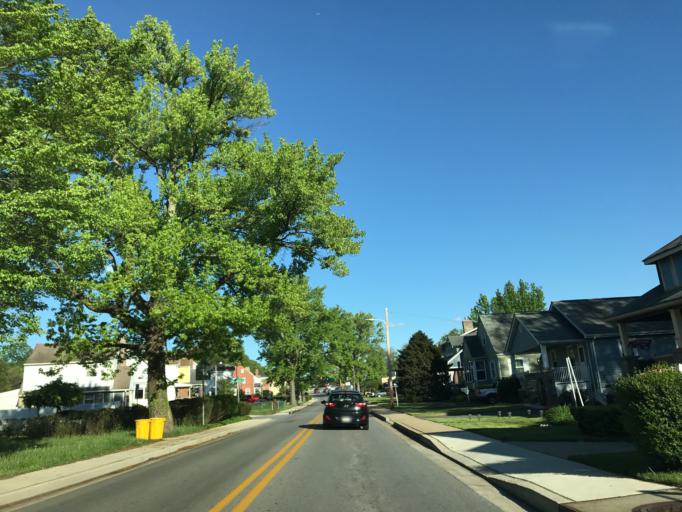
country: US
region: Maryland
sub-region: Baltimore County
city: Parkville
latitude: 39.3768
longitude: -76.5490
